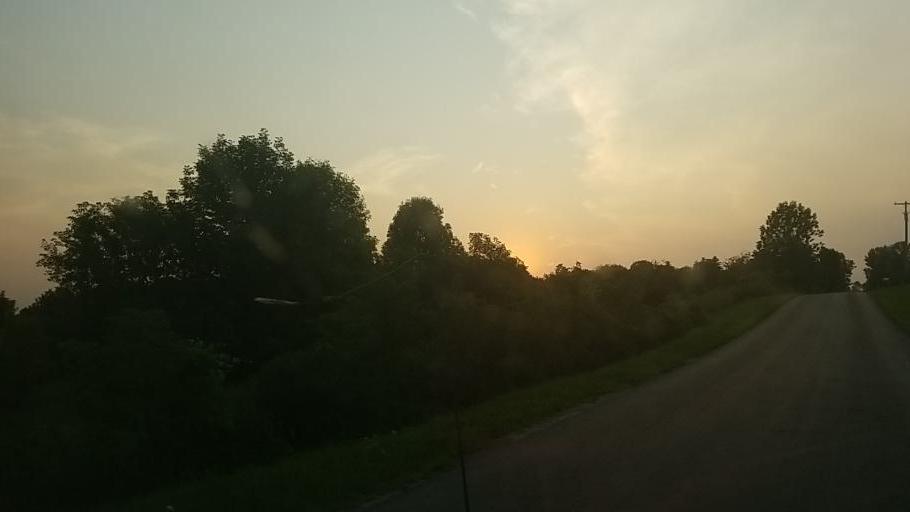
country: US
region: New York
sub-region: Montgomery County
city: Fonda
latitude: 42.9138
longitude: -74.3991
